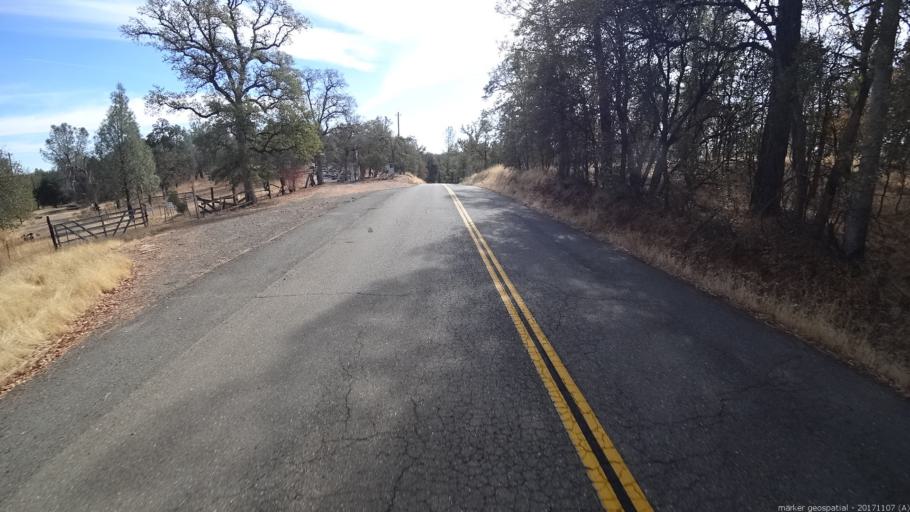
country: US
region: California
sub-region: Shasta County
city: Shasta
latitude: 40.4124
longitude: -122.5212
